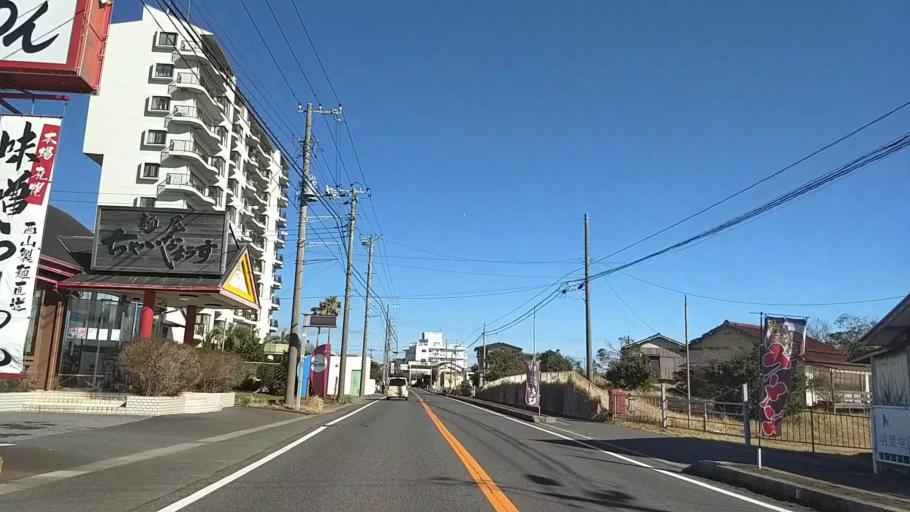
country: JP
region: Chiba
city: Tateyama
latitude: 34.9767
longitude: 139.9644
